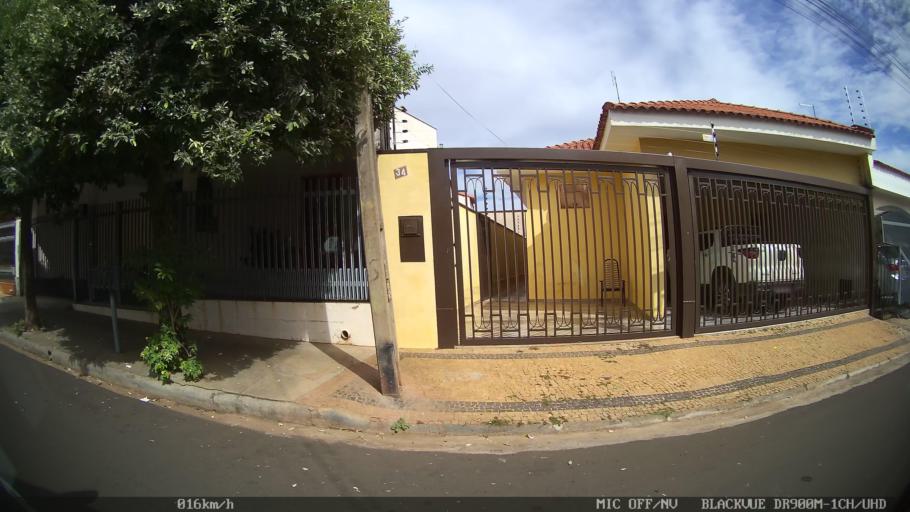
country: BR
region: Sao Paulo
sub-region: Catanduva
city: Catanduva
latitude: -21.1465
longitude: -48.9658
